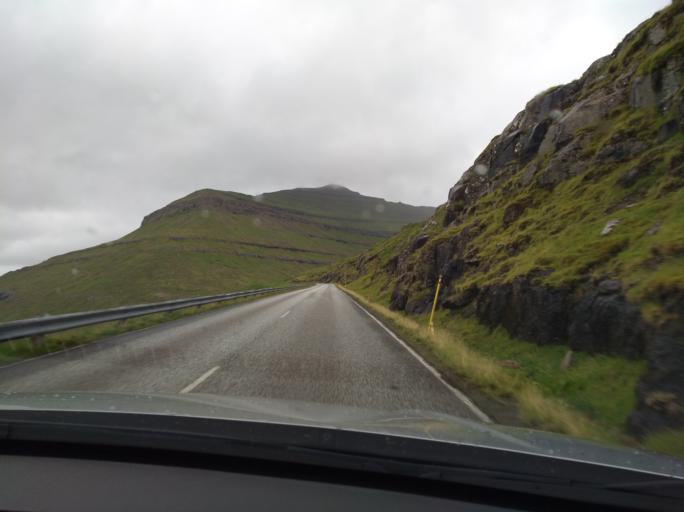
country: FO
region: Eysturoy
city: Fuglafjordur
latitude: 62.2199
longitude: -6.8698
